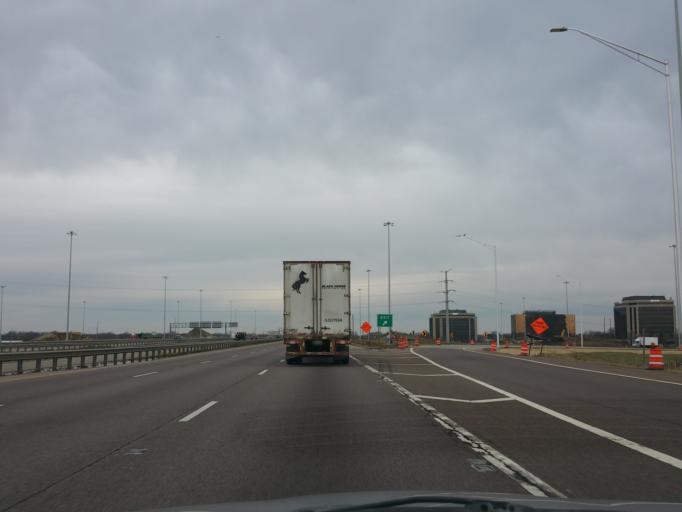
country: US
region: Illinois
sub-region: Cook County
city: Rolling Meadows
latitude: 42.0532
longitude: -88.0284
